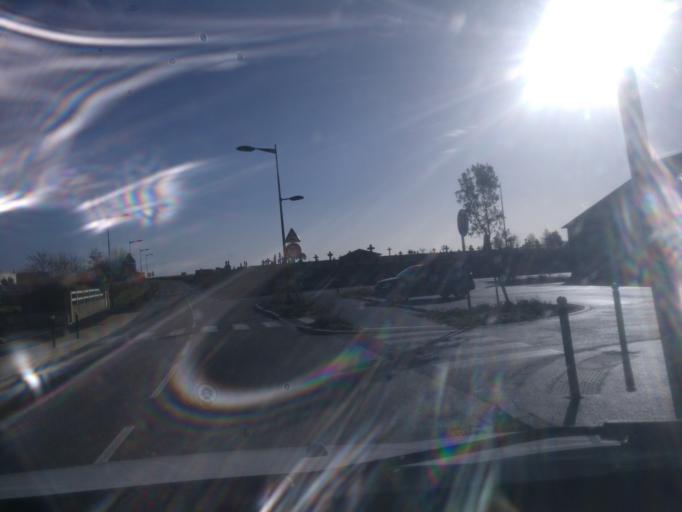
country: FR
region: Brittany
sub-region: Departement d'Ille-et-Vilaine
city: Pleine-Fougeres
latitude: 48.5333
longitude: -1.5591
